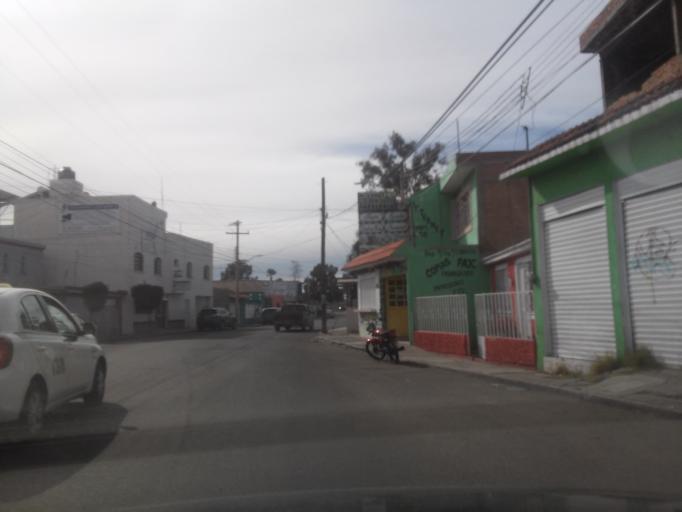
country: MX
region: Durango
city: Victoria de Durango
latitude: 24.0076
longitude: -104.6570
